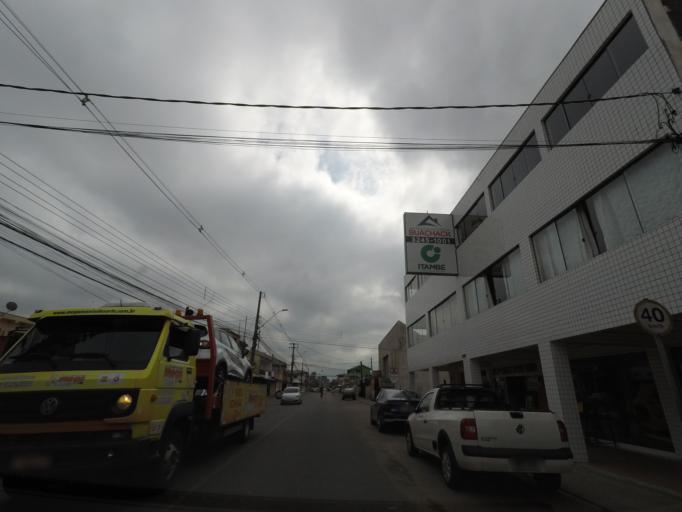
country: BR
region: Parana
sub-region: Curitiba
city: Curitiba
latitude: -25.4987
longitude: -49.3379
